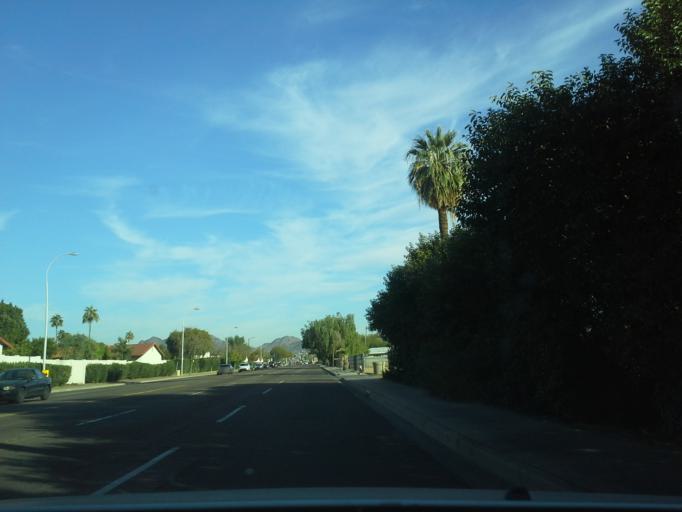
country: US
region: Arizona
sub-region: Maricopa County
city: Glendale
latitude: 33.5675
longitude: -112.0876
